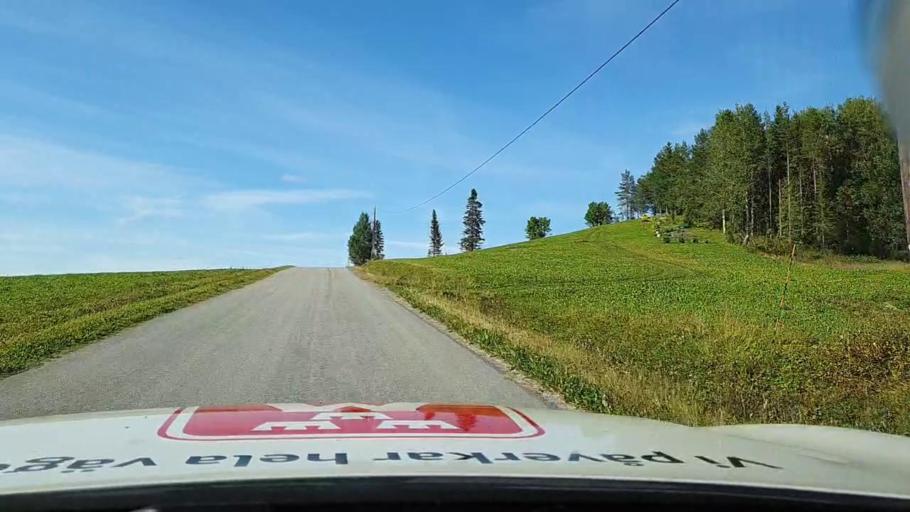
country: SE
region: Jaemtland
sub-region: OEstersunds Kommun
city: Lit
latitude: 63.6404
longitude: 14.9583
